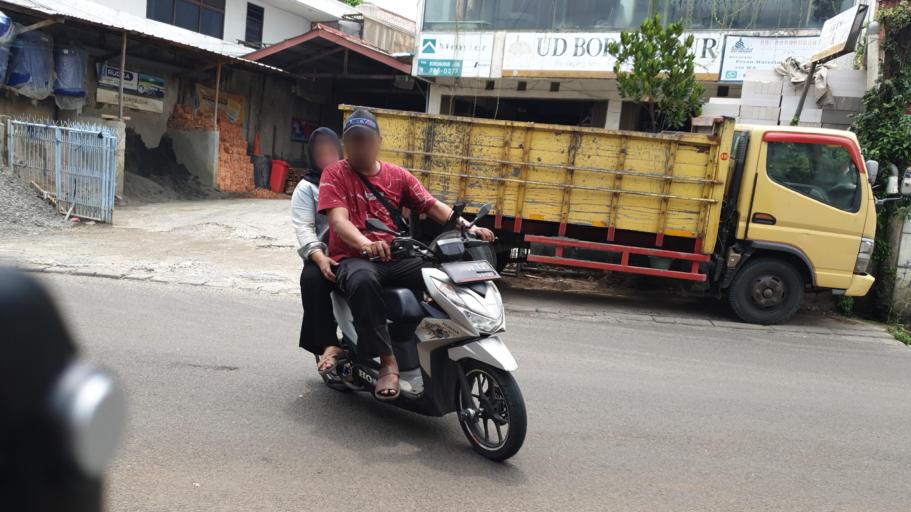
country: ID
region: Banten
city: South Tangerang
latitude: -6.2820
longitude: 106.7935
